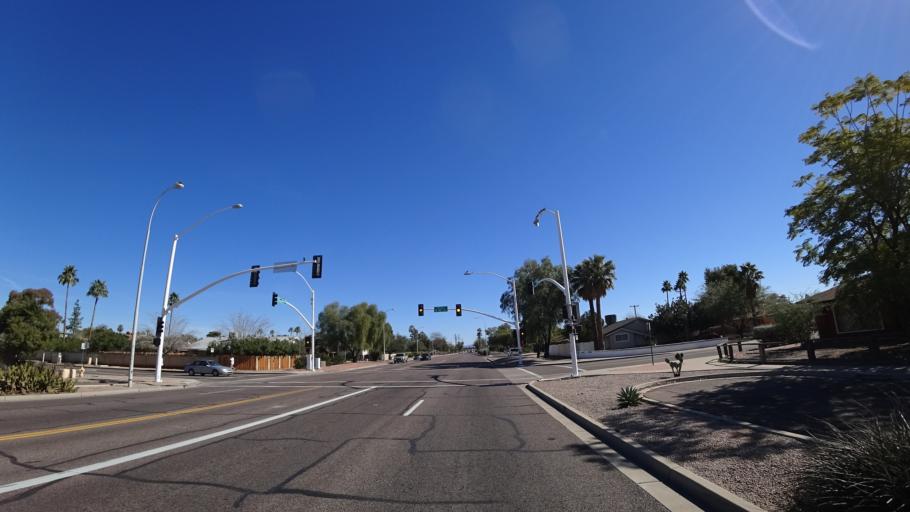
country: US
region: Arizona
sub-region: Maricopa County
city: Scottsdale
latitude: 33.5094
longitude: -111.8963
